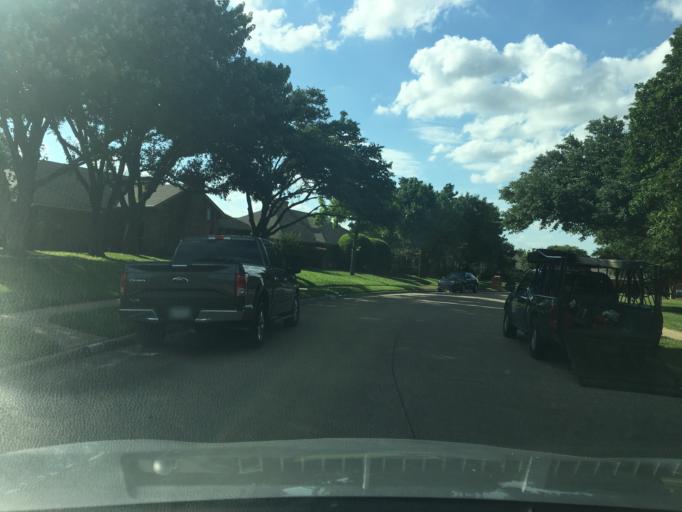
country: US
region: Texas
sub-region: Dallas County
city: Garland
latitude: 32.9387
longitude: -96.6800
